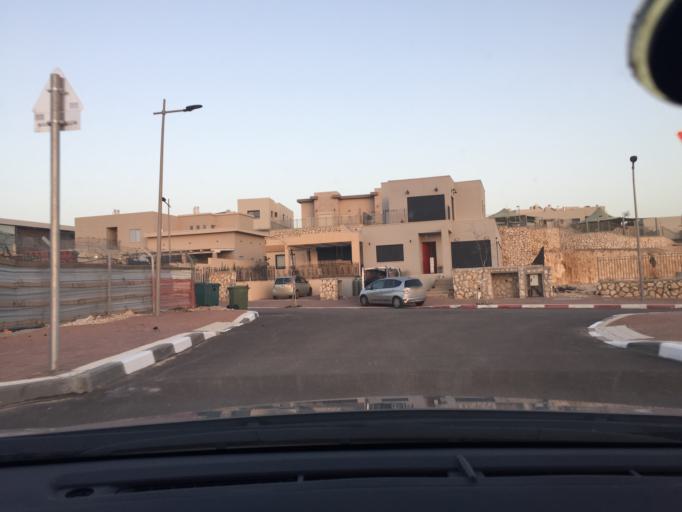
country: PS
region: West Bank
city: Rafat
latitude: 32.0676
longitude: 35.0464
